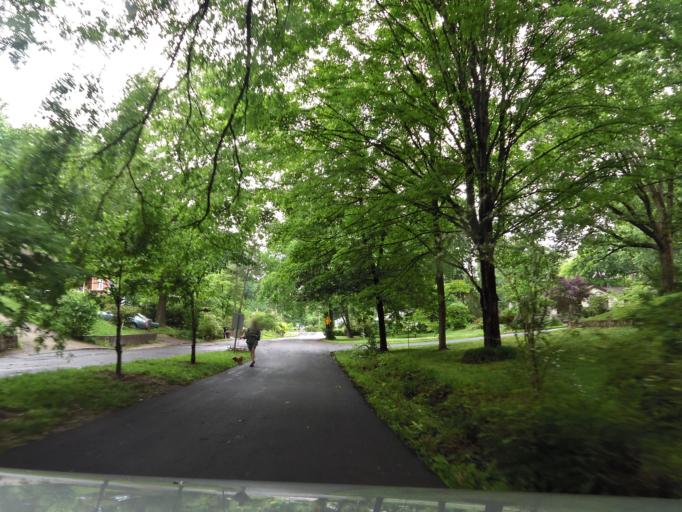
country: US
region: Tennessee
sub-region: Knox County
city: Knoxville
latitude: 36.0028
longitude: -83.9025
